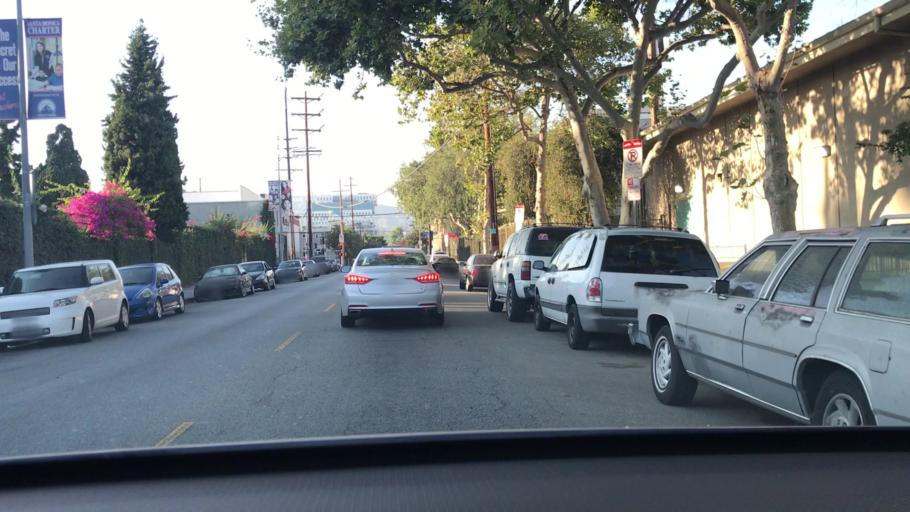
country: US
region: California
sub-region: Los Angeles County
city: Hollywood
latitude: 34.0896
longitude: -118.3157
